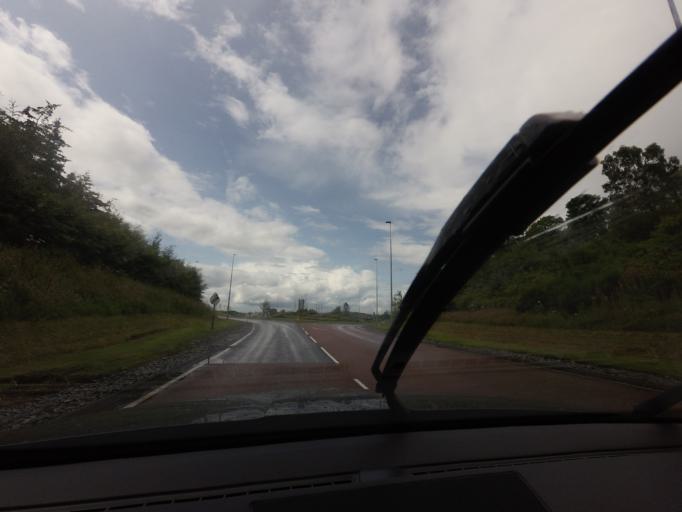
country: GB
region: Scotland
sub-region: Moray
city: Fochabers
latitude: 57.6225
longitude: -3.1136
